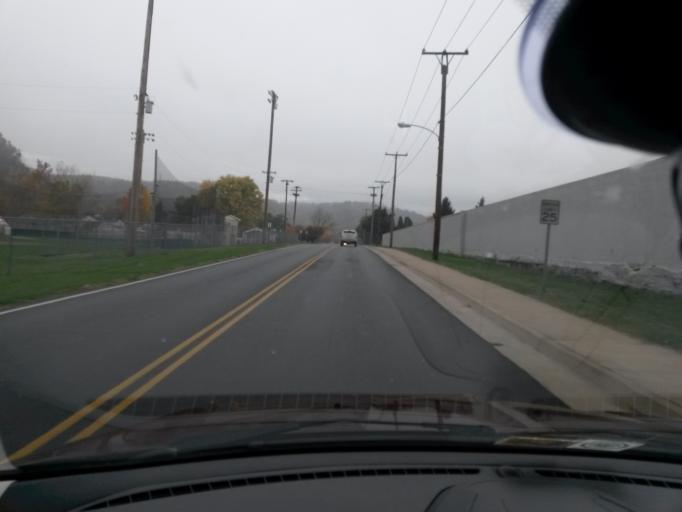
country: US
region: Virginia
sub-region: City of Covington
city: Covington
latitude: 37.7829
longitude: -79.9926
